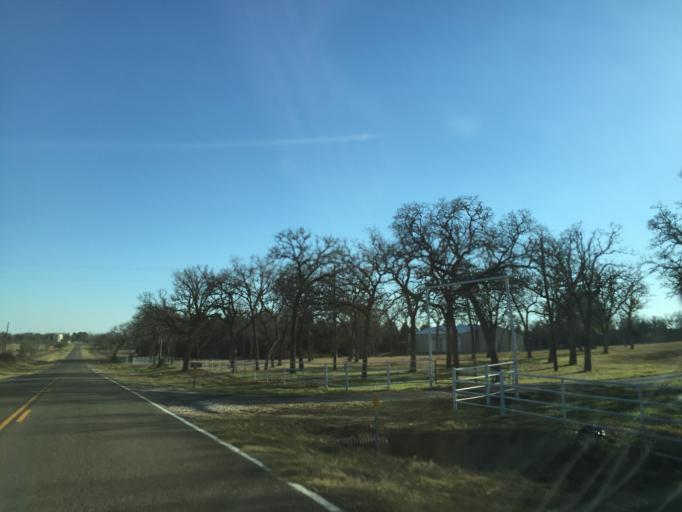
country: US
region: Texas
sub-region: Bastrop County
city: Elgin
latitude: 30.3925
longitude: -97.2463
